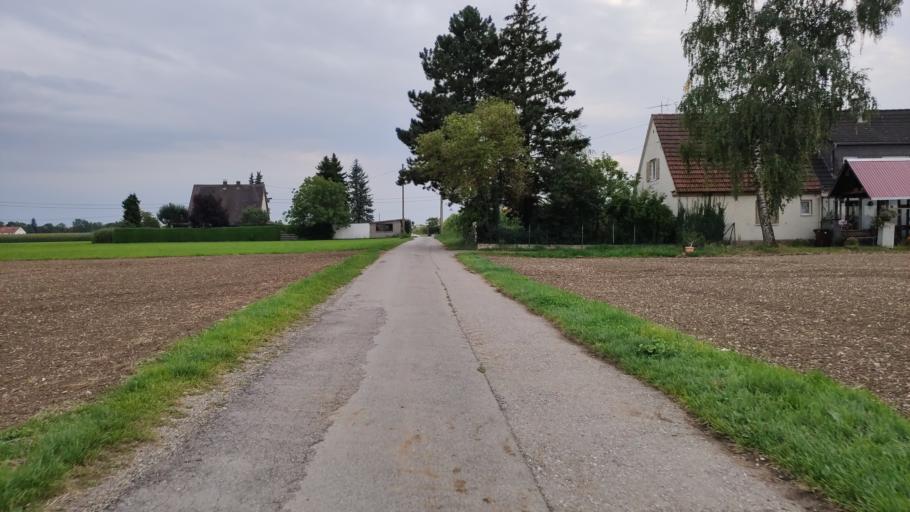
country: DE
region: Bavaria
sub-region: Swabia
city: Konigsbrunn
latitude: 48.2632
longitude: 10.8803
